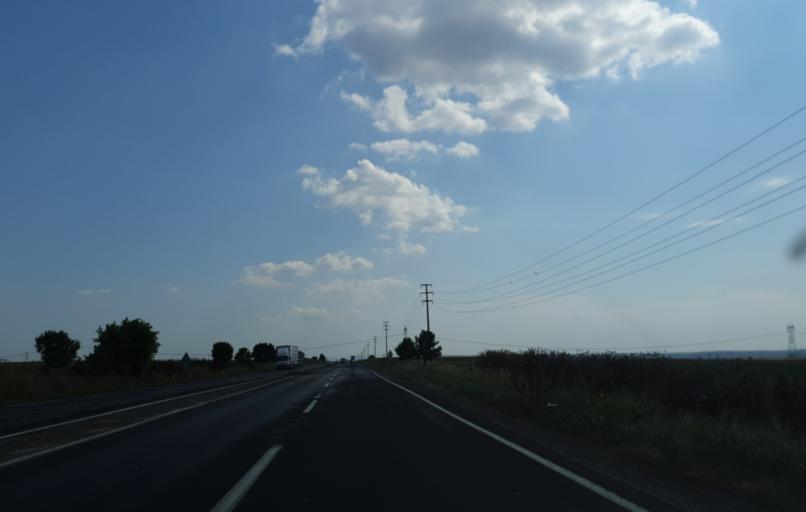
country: TR
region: Kirklareli
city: Buyukkaristiran
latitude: 41.2401
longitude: 27.5370
